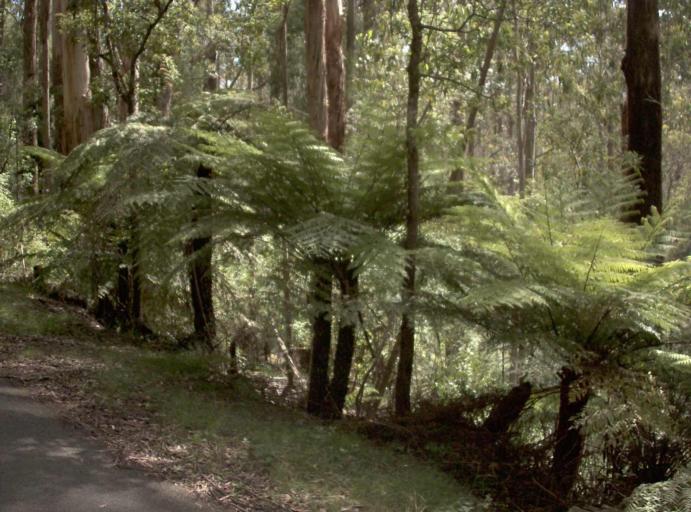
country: AU
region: Victoria
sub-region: Latrobe
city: Moe
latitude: -37.8374
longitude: 146.2050
